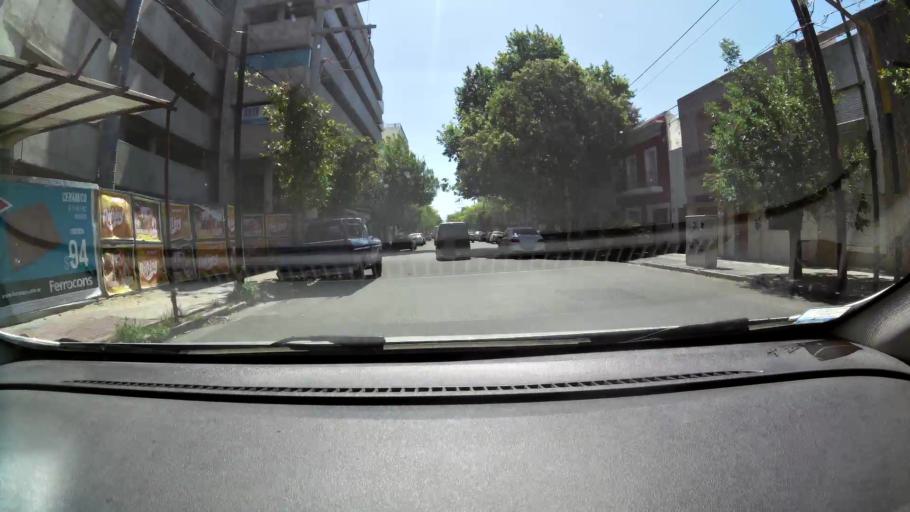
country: AR
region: Cordoba
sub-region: Departamento de Capital
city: Cordoba
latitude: -31.3972
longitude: -64.1894
